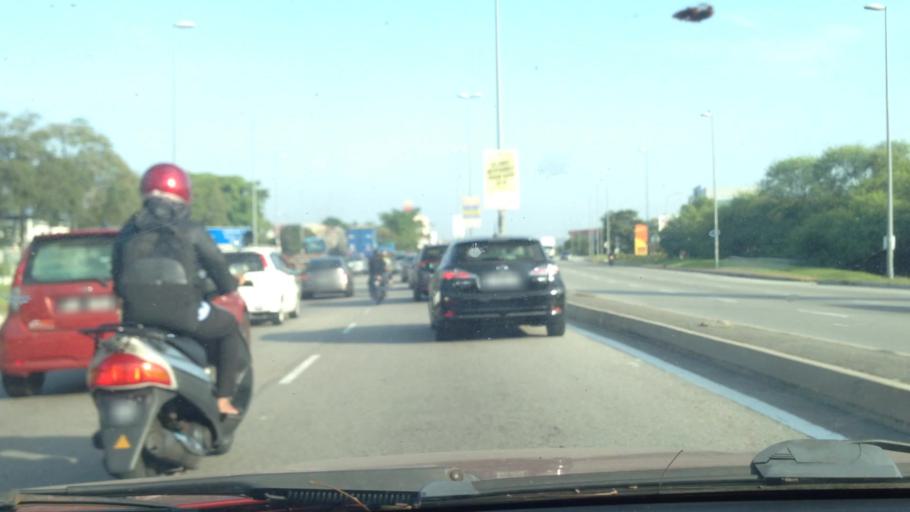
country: MY
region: Selangor
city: Subang Jaya
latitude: 3.0438
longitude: 101.5462
